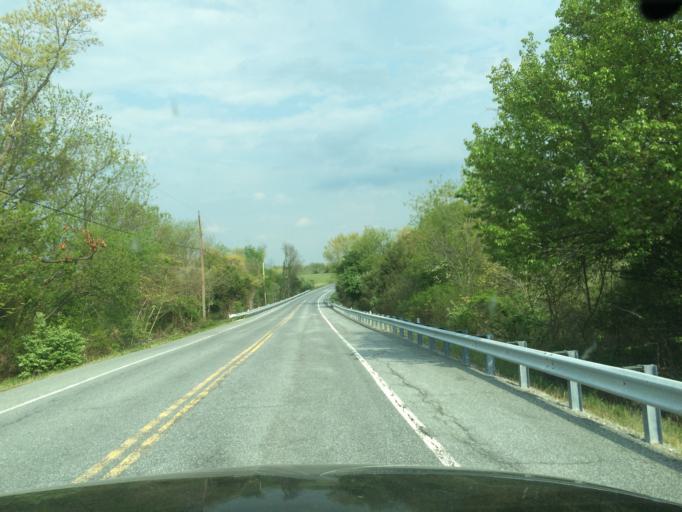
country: US
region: Maryland
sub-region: Carroll County
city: Eldersburg
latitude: 39.4355
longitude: -77.0145
